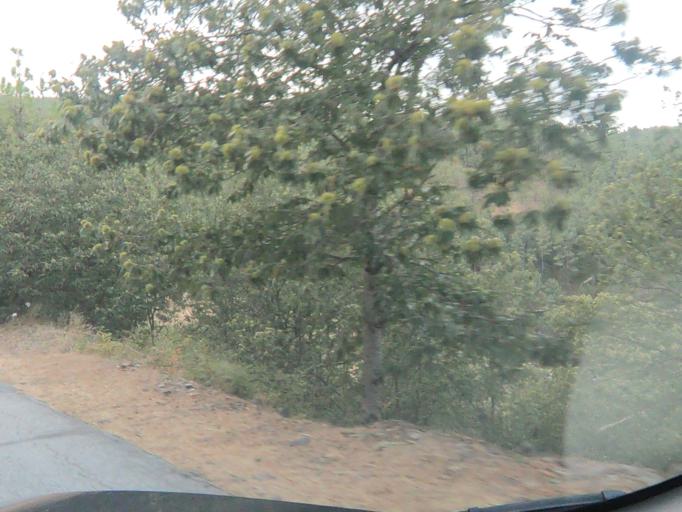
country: PT
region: Vila Real
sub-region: Santa Marta de Penaguiao
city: Santa Marta de Penaguiao
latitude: 41.2414
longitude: -7.8525
